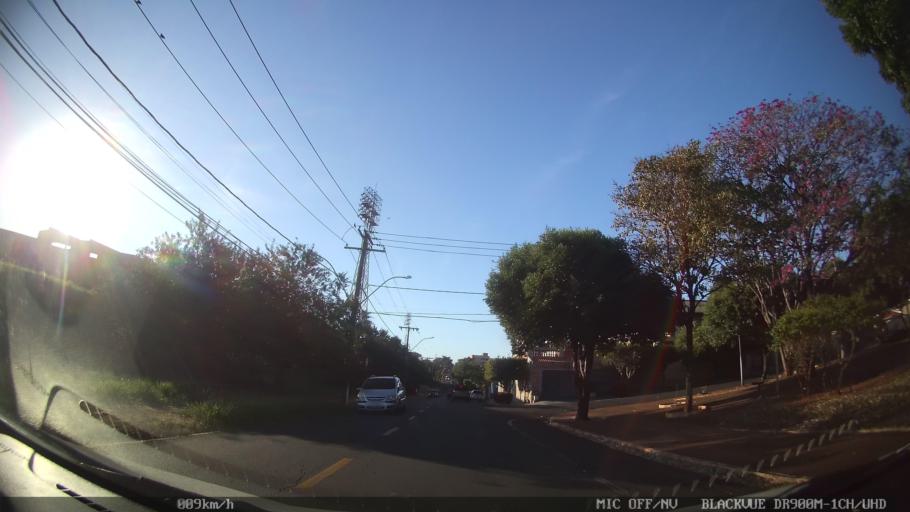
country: BR
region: Sao Paulo
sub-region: Sao Jose Do Rio Preto
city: Sao Jose do Rio Preto
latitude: -20.7981
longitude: -49.3578
